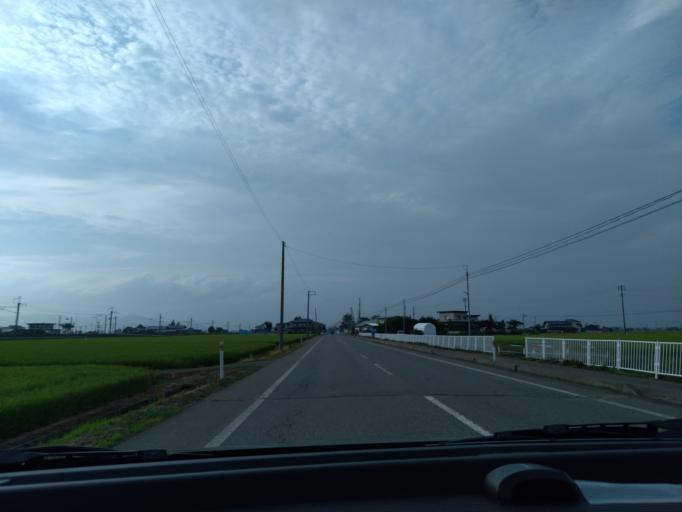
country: JP
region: Akita
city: Omagari
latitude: 39.3958
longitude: 140.5222
